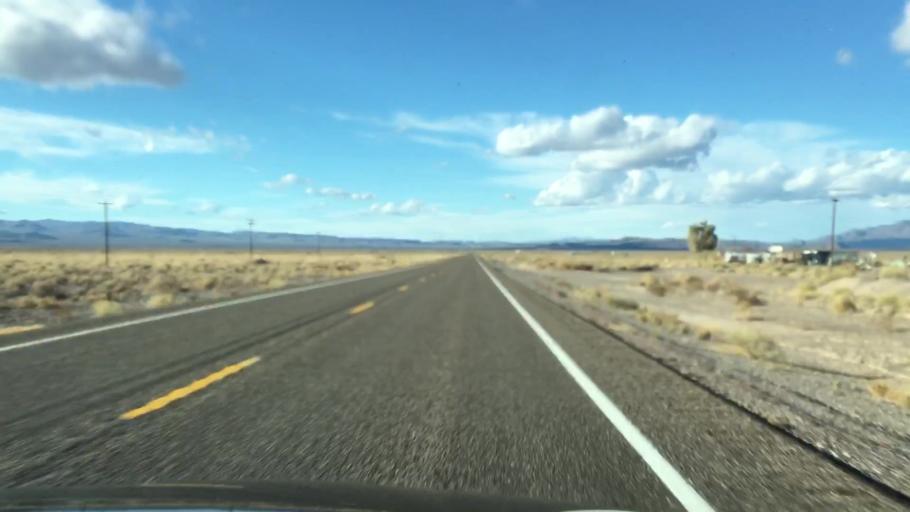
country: US
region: Nevada
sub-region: Nye County
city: Beatty
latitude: 37.2493
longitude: -117.0030
